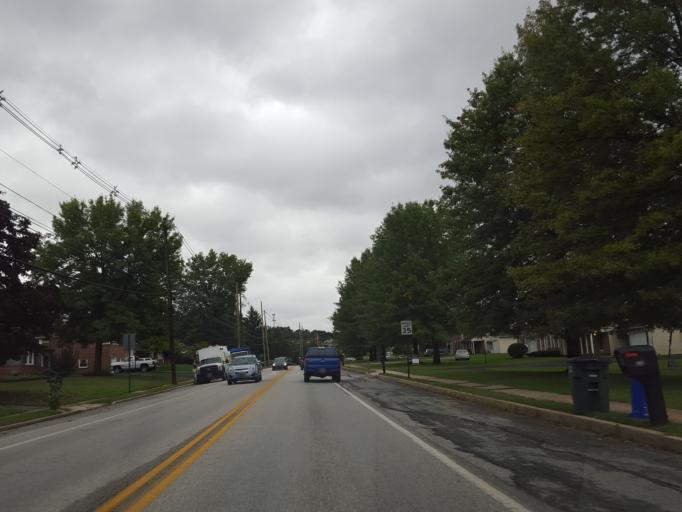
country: US
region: Pennsylvania
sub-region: York County
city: East York
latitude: 39.9631
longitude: -76.6810
